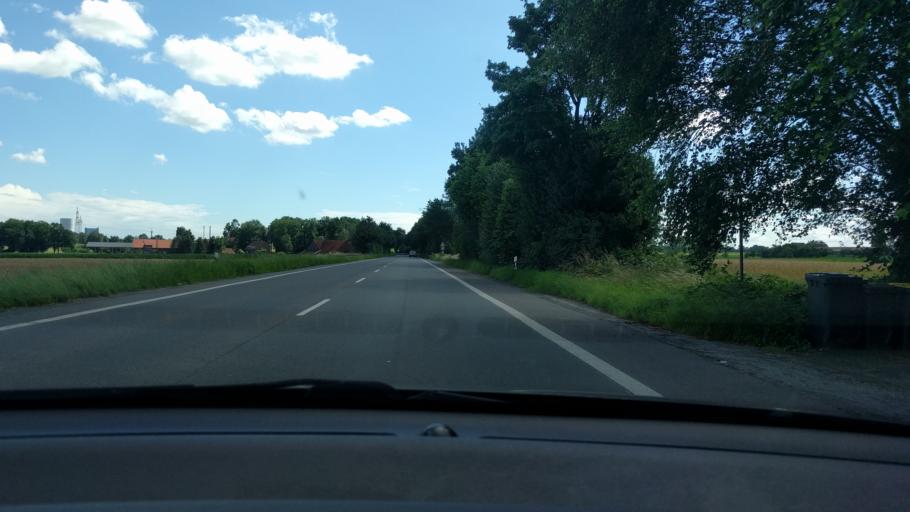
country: DE
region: North Rhine-Westphalia
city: Datteln
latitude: 51.6759
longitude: 7.3274
